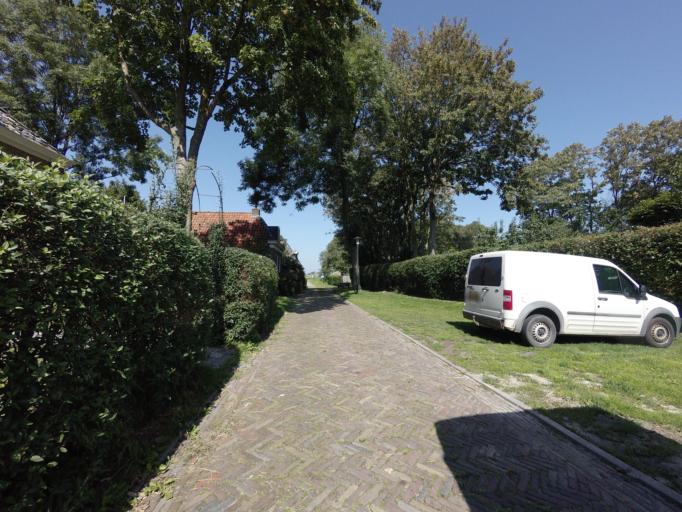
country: NL
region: Friesland
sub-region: Gemeente Dongeradeel
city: Ternaard
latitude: 53.3722
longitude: 5.9966
